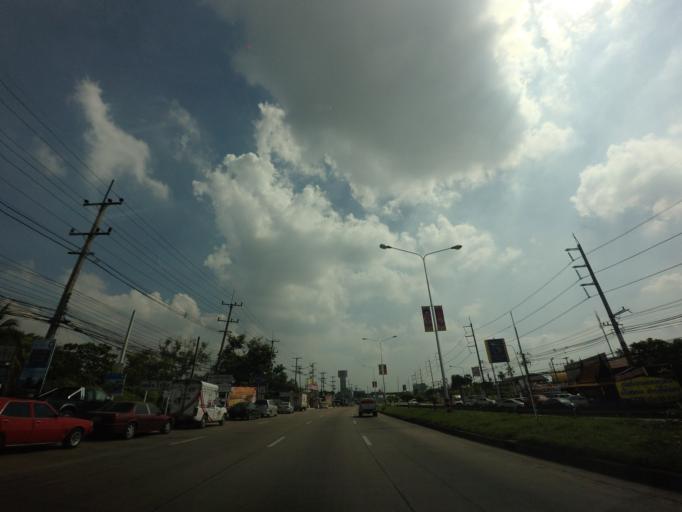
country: TH
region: Nakhon Pathom
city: Sam Phran
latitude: 13.7411
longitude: 100.2395
